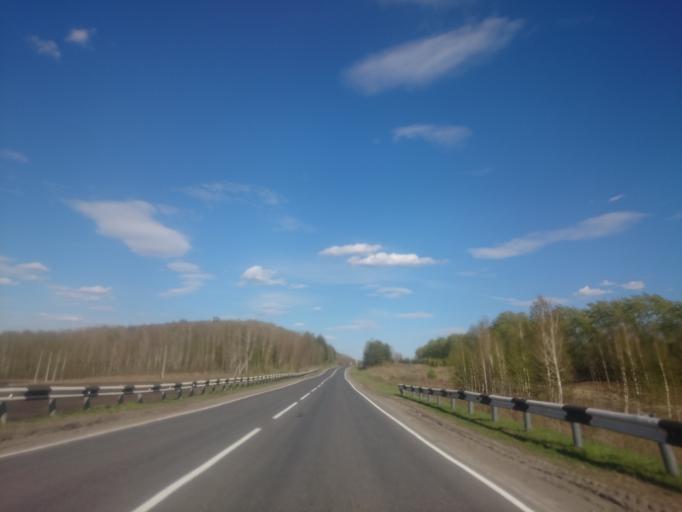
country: RU
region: Sverdlovsk
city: Lesnoy
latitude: 57.6199
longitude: 63.2235
